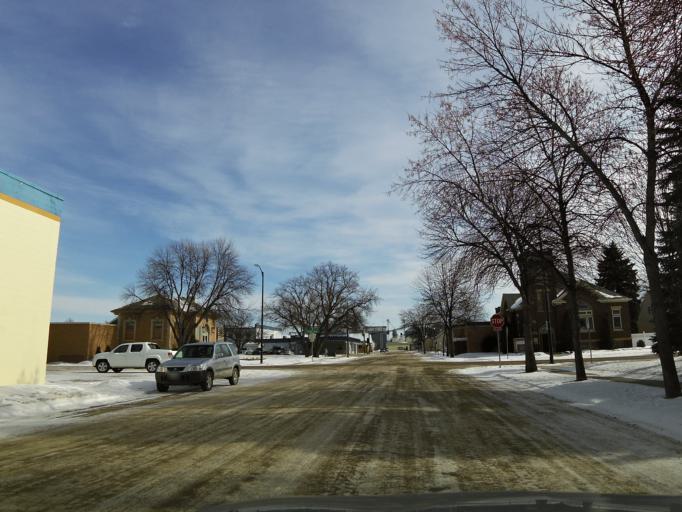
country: US
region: North Dakota
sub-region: Walsh County
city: Grafton
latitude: 48.4175
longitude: -97.4133
